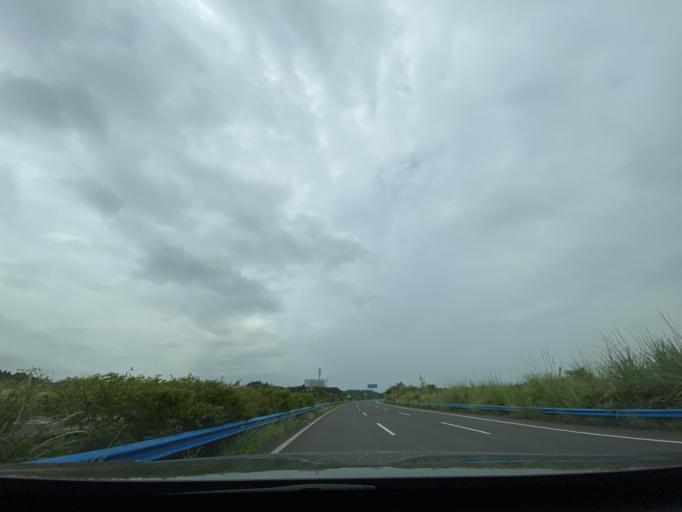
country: CN
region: Sichuan
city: Jiancheng
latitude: 30.4290
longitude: 104.4002
